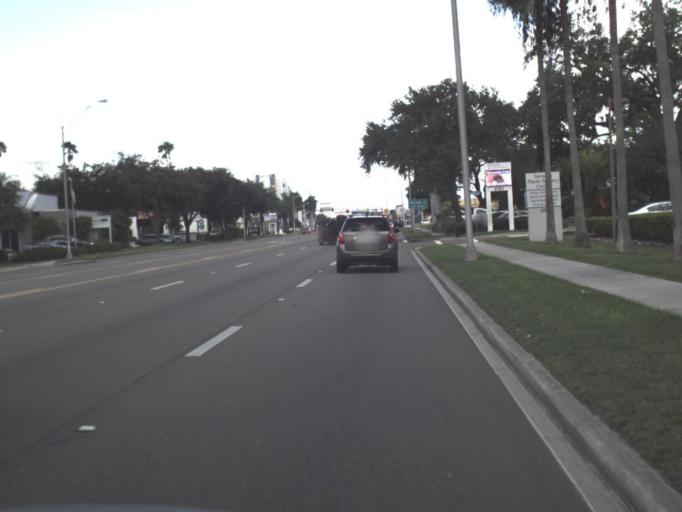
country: US
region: Florida
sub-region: Sarasota County
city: Southgate
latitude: 27.3134
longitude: -82.5297
